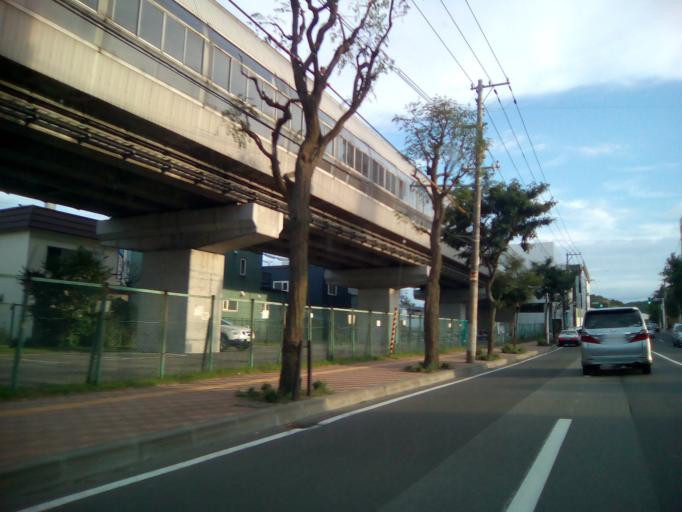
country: JP
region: Hokkaido
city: Sapporo
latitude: 43.0074
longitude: 141.3649
